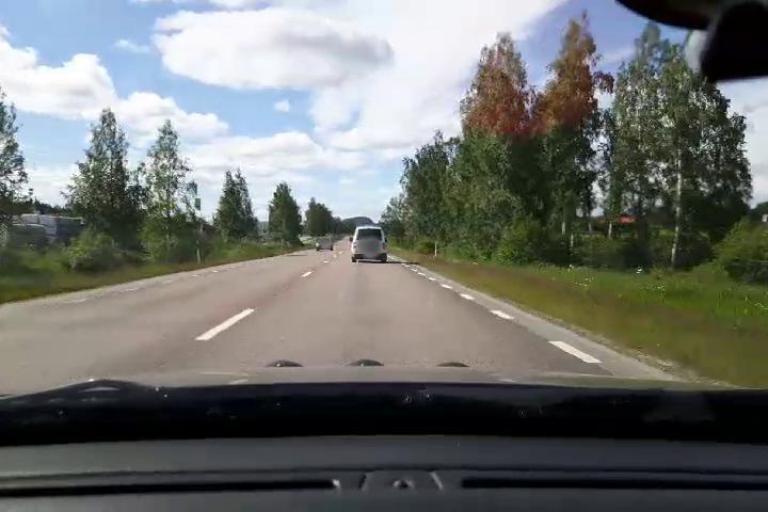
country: SE
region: Gaevleborg
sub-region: Bollnas Kommun
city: Bollnas
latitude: 61.3340
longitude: 16.4049
